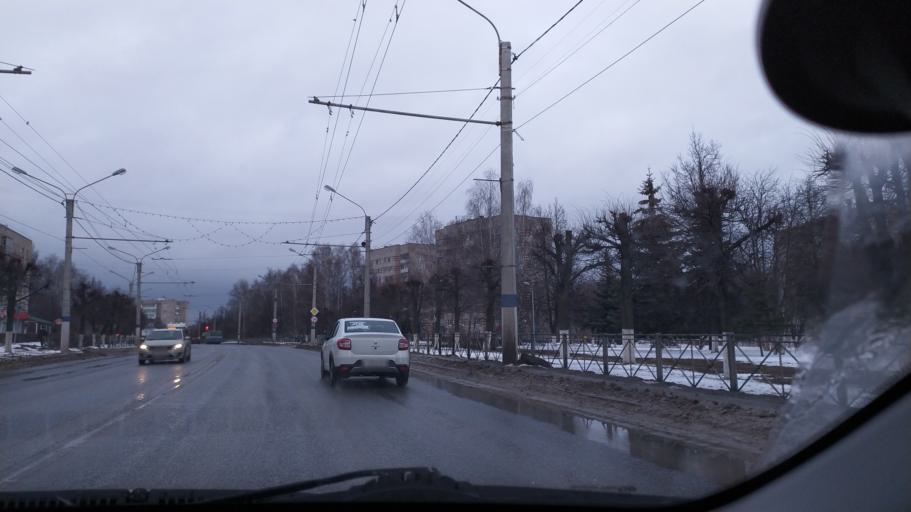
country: RU
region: Chuvashia
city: Novocheboksarsk
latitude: 56.1161
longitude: 47.4905
